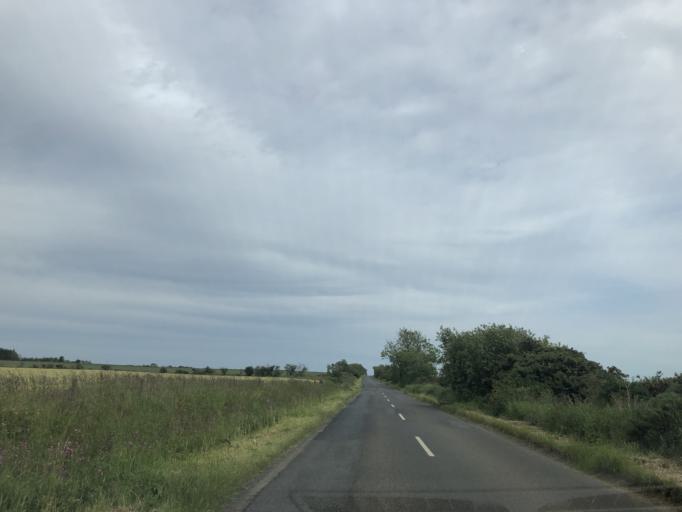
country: GB
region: Scotland
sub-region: Fife
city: Anstruther
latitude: 56.2600
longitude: -2.6815
